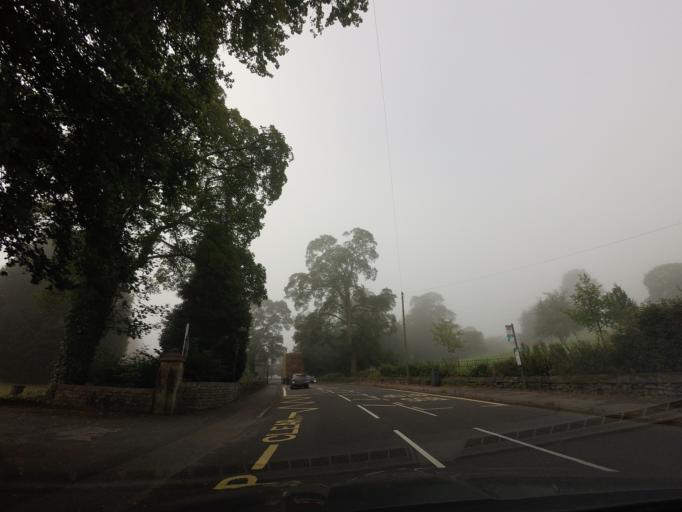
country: GB
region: England
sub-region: Derbyshire
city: Bakewell
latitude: 53.2193
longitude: -1.6730
